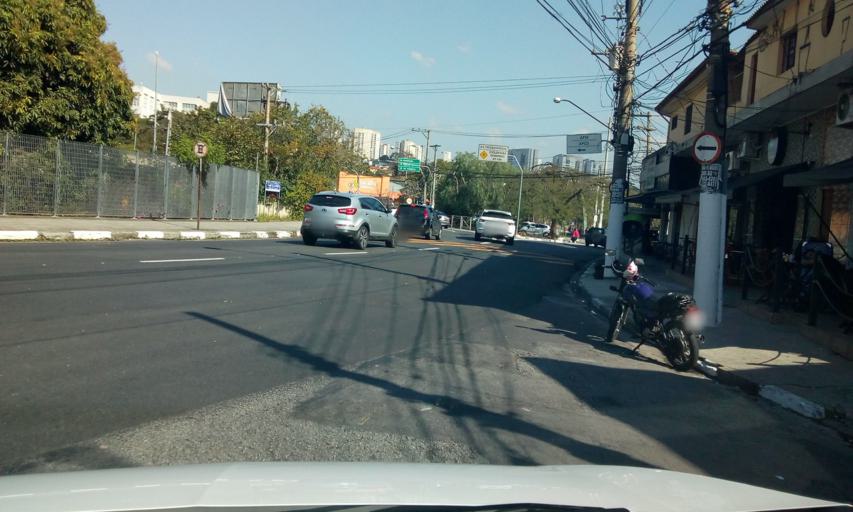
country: BR
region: Sao Paulo
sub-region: Osasco
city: Osasco
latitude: -23.5467
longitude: -46.7751
